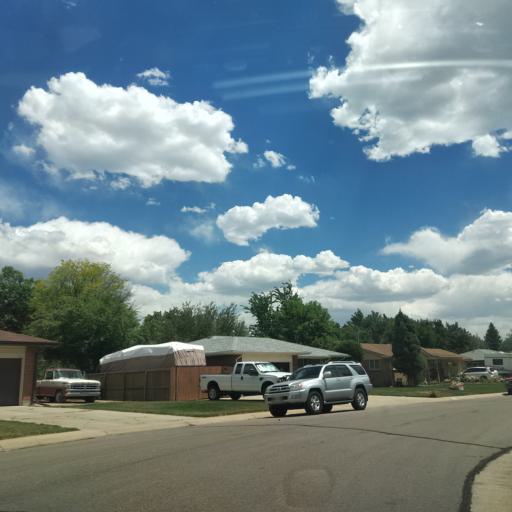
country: US
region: Colorado
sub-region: Jefferson County
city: Lakewood
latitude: 39.6871
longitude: -105.0948
